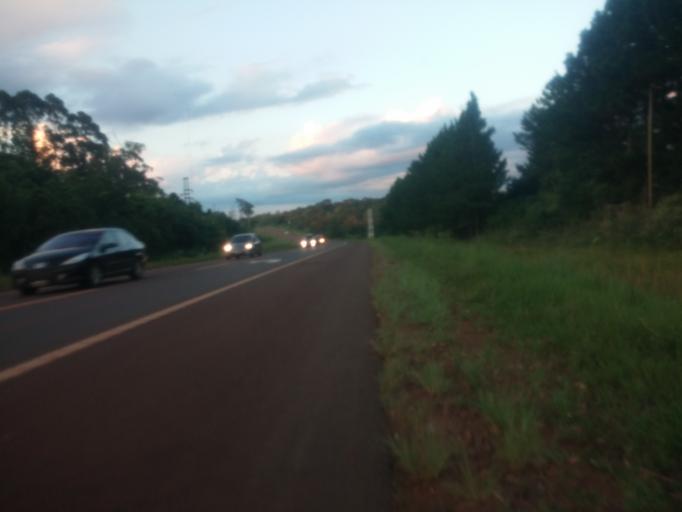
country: AR
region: Misiones
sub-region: Departamento de Obera
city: Obera
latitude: -27.4492
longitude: -55.0829
